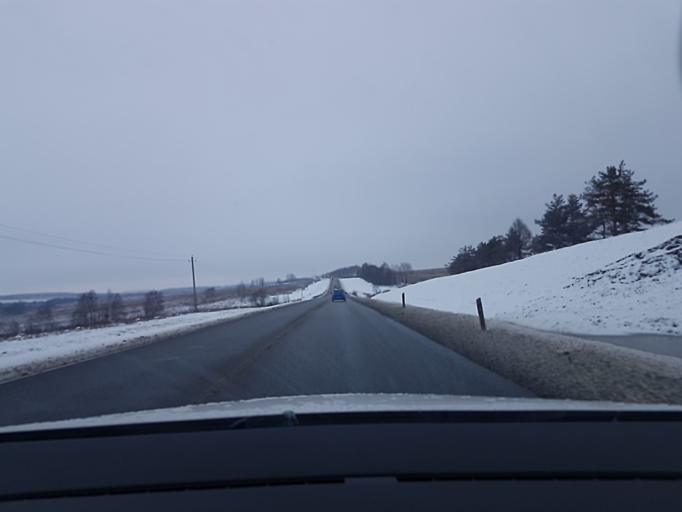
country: RU
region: Moskovskaya
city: Ozherel'ye
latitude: 54.7276
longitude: 38.2679
